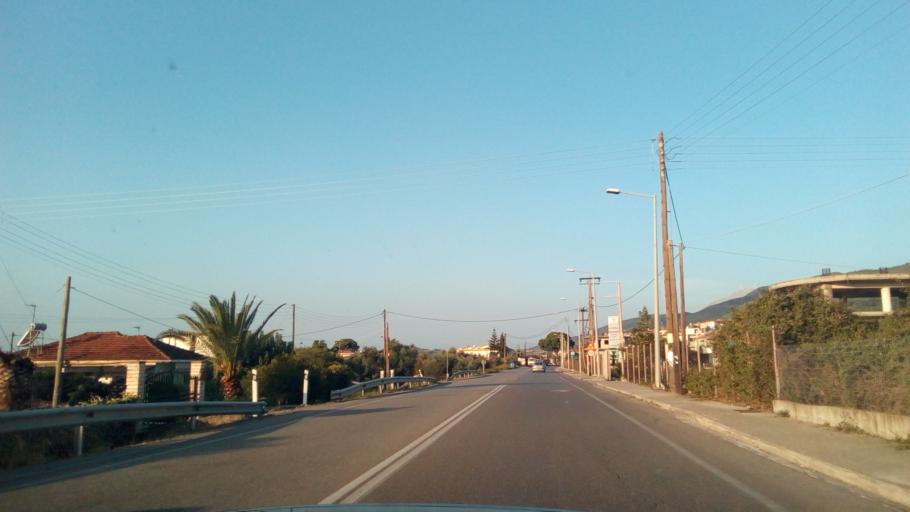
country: GR
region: West Greece
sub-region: Nomos Aitolias kai Akarnanias
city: Nafpaktos
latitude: 38.3826
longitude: 21.8044
